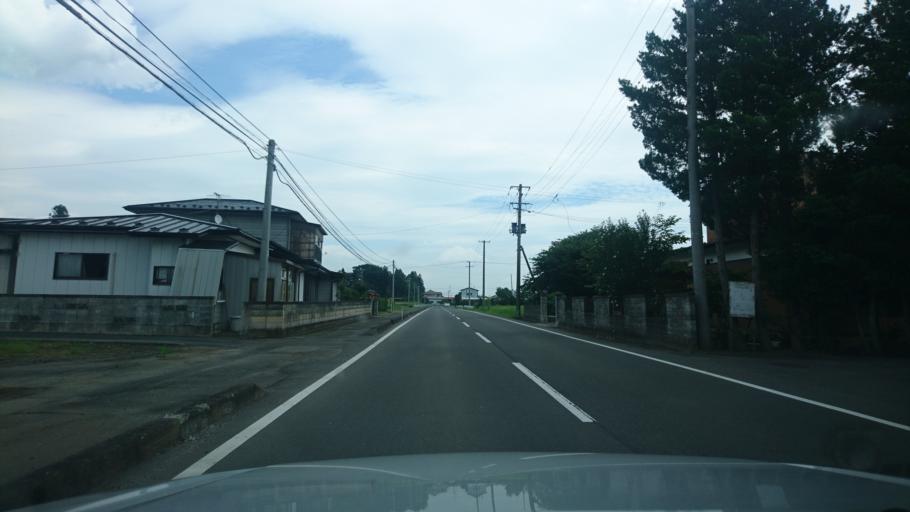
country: JP
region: Iwate
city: Ichinoseki
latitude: 38.8036
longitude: 140.9641
